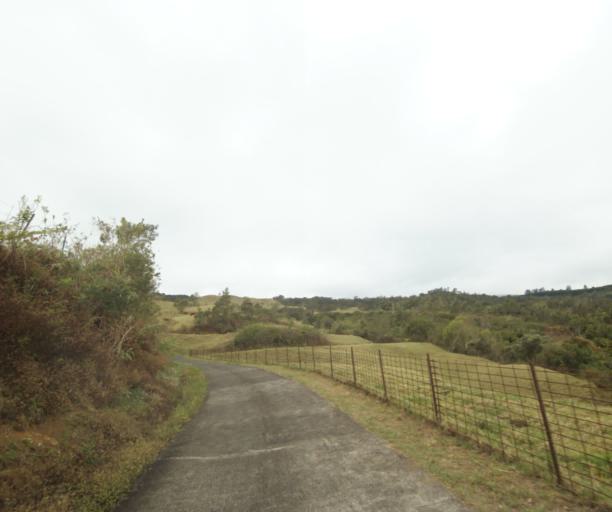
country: RE
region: Reunion
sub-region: Reunion
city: Saint-Paul
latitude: -21.0173
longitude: 55.3480
